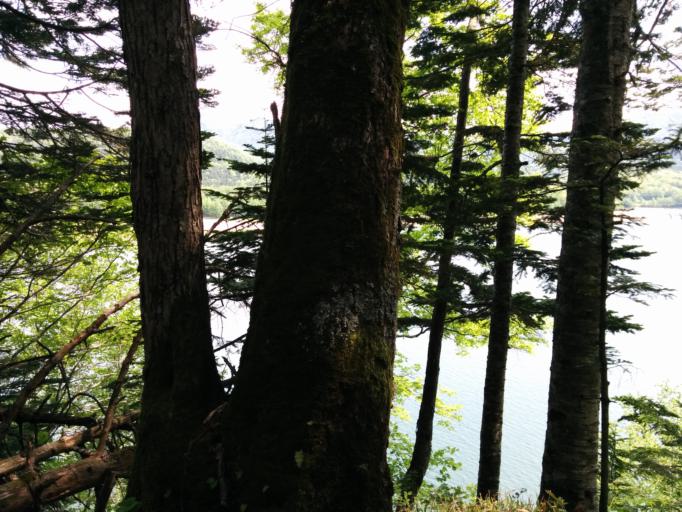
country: JP
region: Hokkaido
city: Otofuke
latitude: 43.4143
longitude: 143.1798
